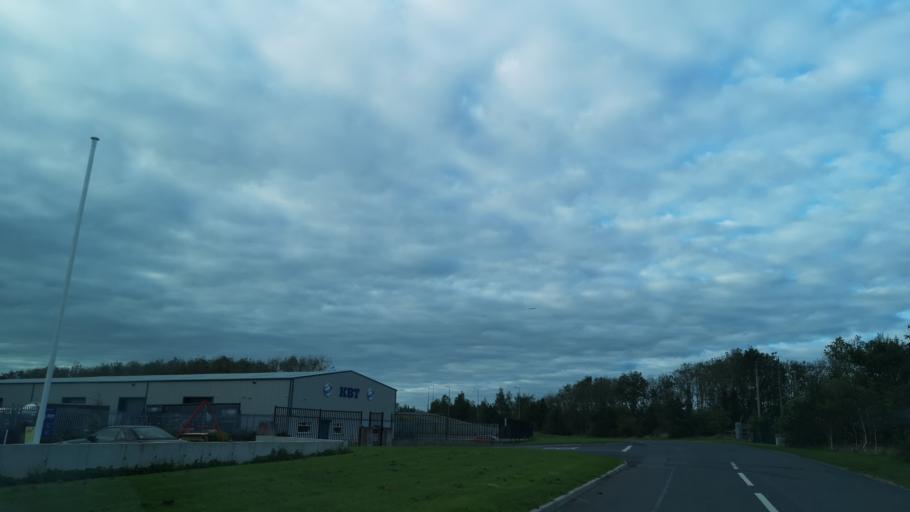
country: IE
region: Connaught
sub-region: County Galway
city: Athenry
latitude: 53.2873
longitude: -8.7551
